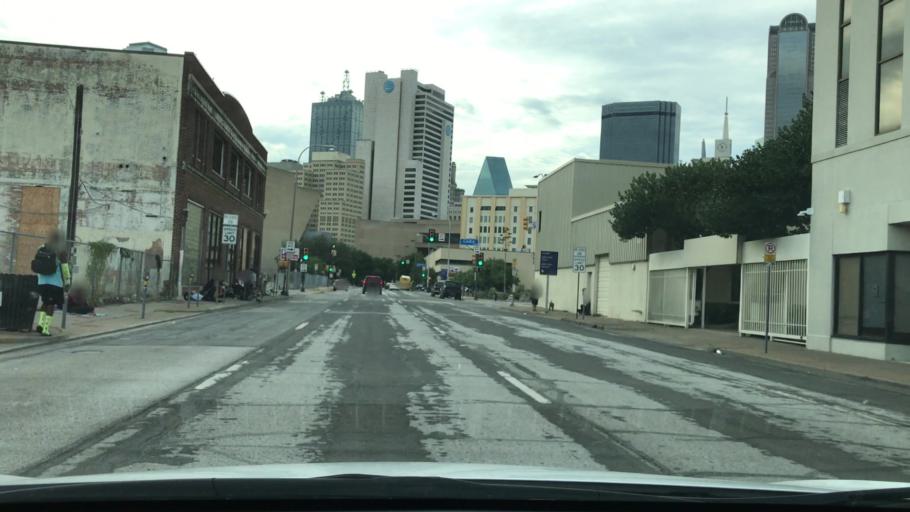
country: US
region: Texas
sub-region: Dallas County
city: Dallas
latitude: 32.7749
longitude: -96.7937
